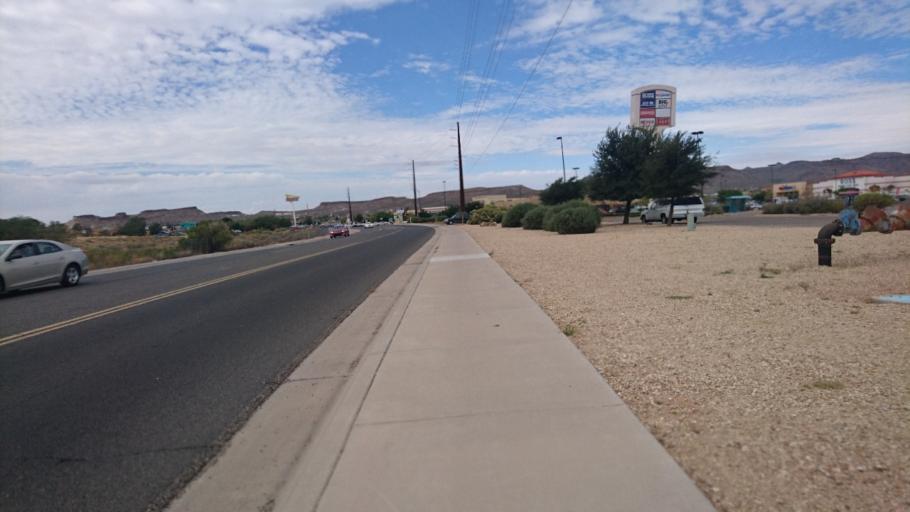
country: US
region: Arizona
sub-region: Mohave County
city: Kingman
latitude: 35.2187
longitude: -114.0325
